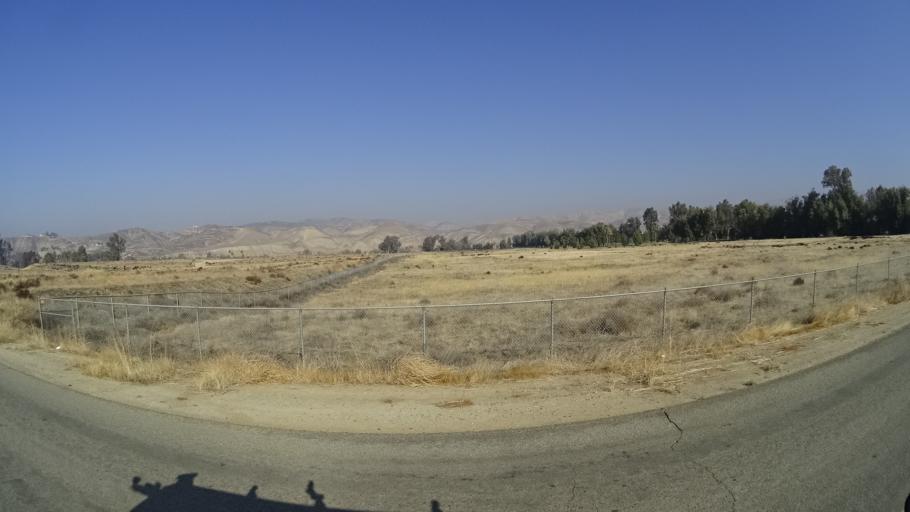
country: US
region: California
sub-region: Kern County
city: Oildale
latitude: 35.4330
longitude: -118.8635
